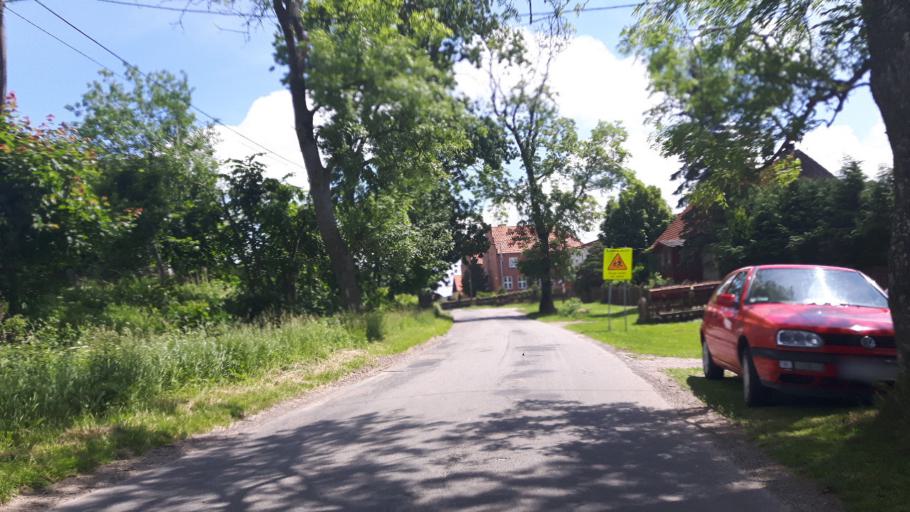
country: PL
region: Pomeranian Voivodeship
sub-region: Powiat slupski
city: Ustka
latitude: 54.5217
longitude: 16.7617
